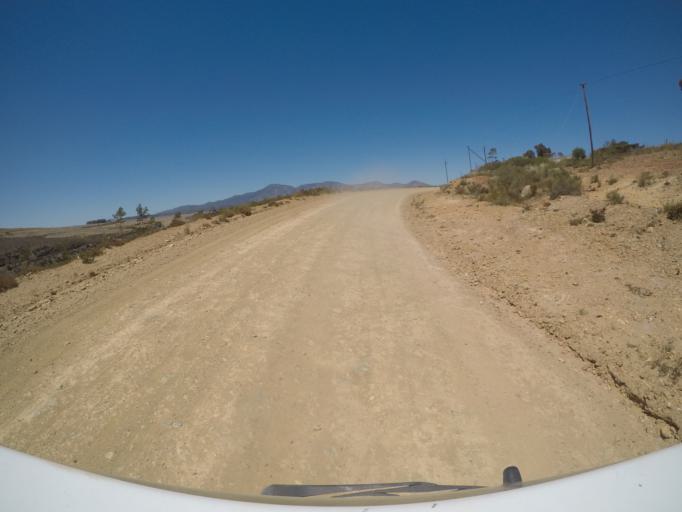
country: ZA
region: Western Cape
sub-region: Overberg District Municipality
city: Hermanus
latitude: -34.2209
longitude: 19.2055
